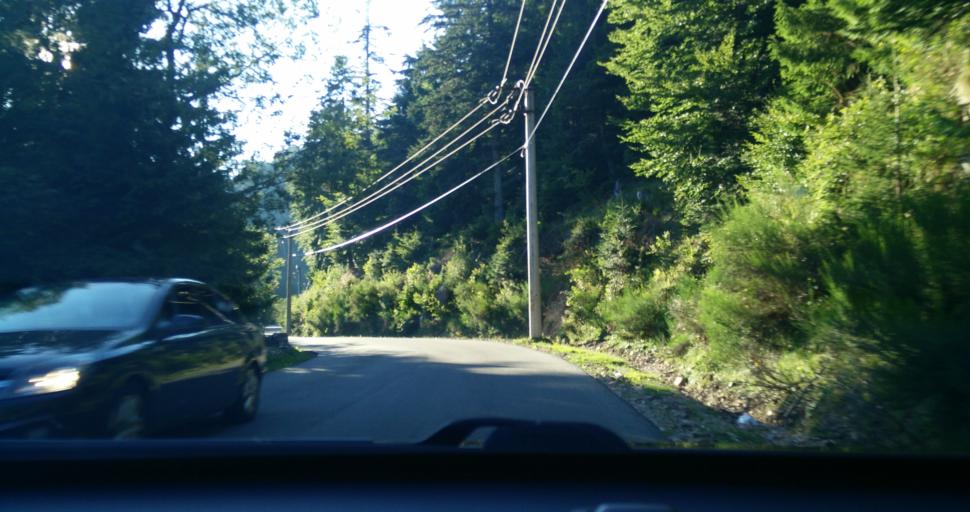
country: RO
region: Bihor
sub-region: Oras Nucet
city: Nucet
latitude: 46.5208
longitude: 22.6396
